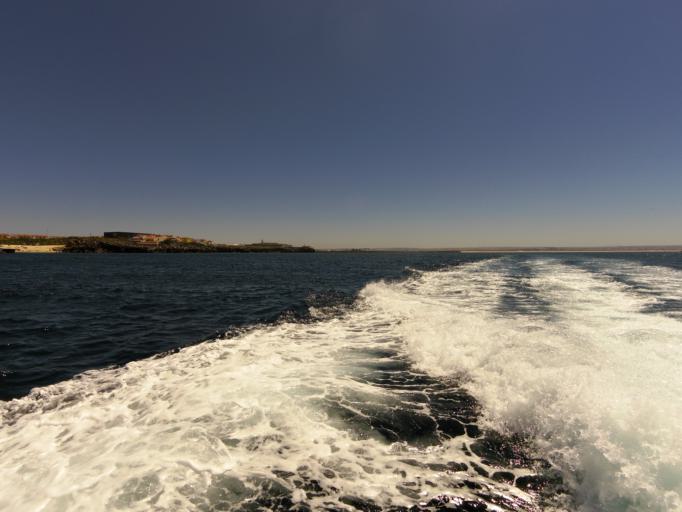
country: PT
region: Leiria
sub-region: Peniche
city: Peniche
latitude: 39.3508
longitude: -9.3916
